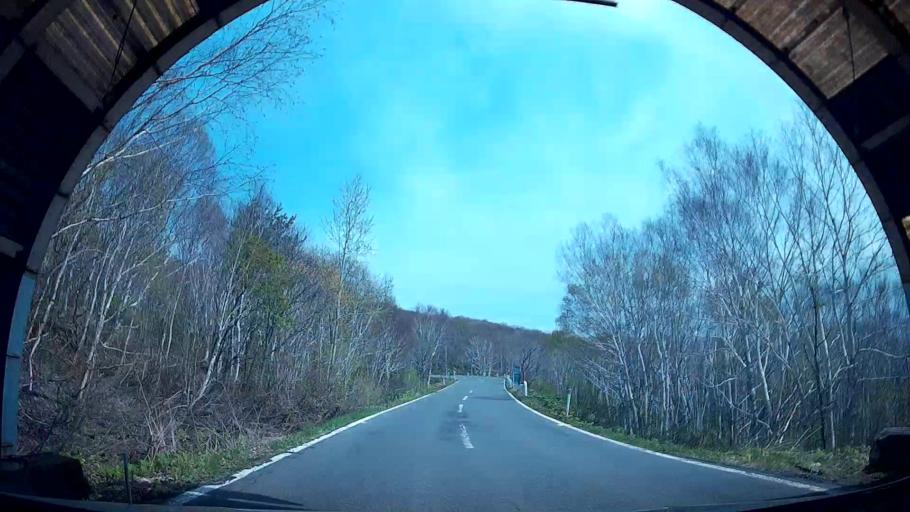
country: JP
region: Iwate
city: Shizukuishi
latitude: 39.9353
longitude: 140.9564
